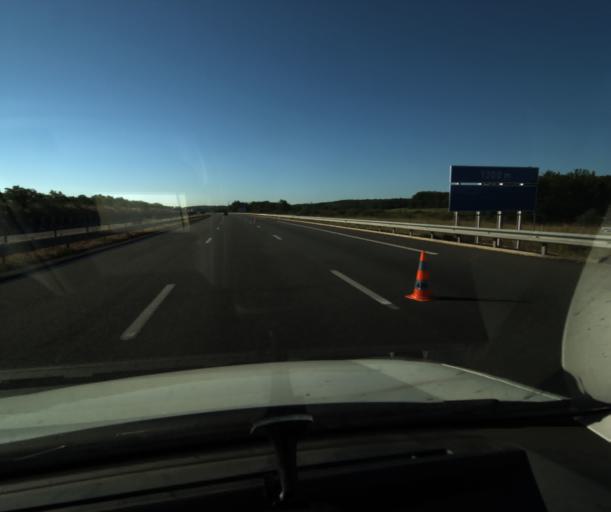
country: FR
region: Midi-Pyrenees
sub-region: Departement du Tarn-et-Garonne
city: Pompignan
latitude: 43.8223
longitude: 1.3473
